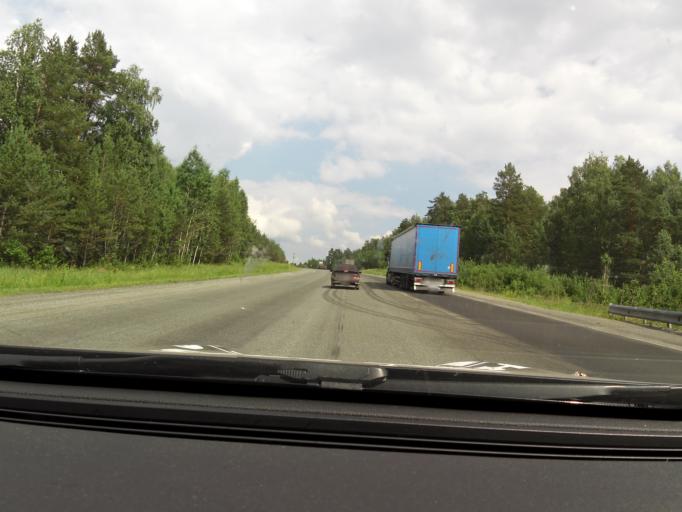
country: RU
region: Sverdlovsk
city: Ufimskiy
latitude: 56.7751
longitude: 58.2440
